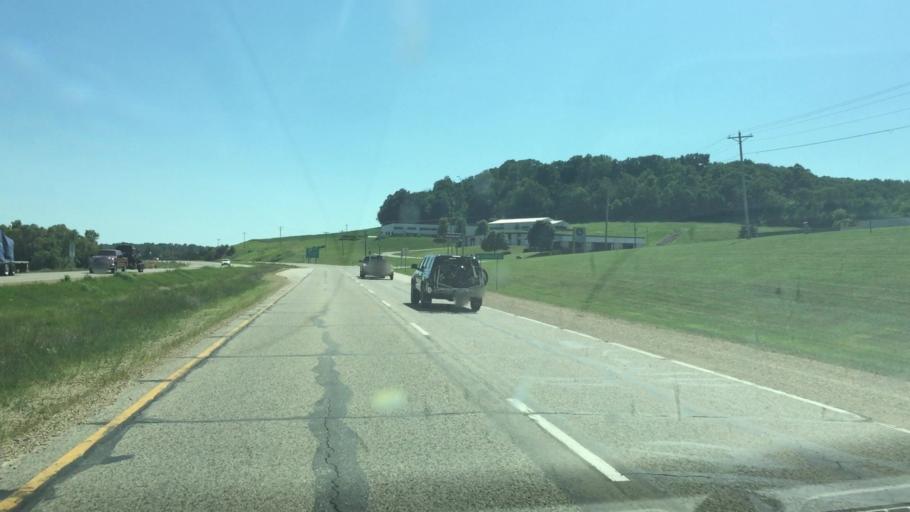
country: US
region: Iowa
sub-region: Dubuque County
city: Dubuque
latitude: 42.4293
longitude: -90.6890
